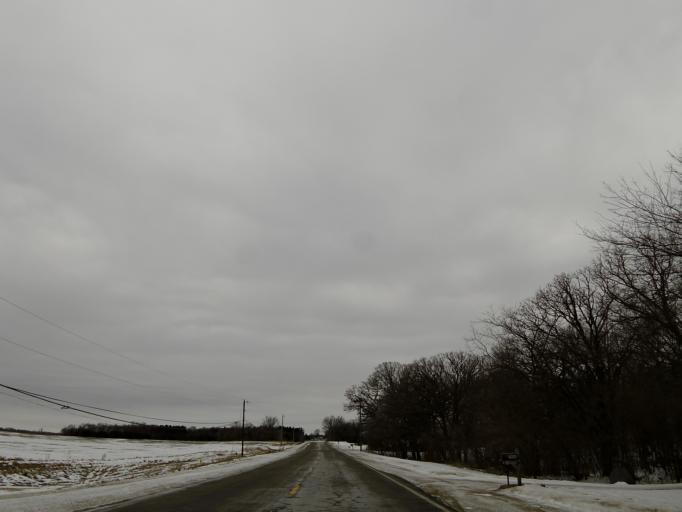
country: US
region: Minnesota
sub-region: Washington County
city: Cottage Grove
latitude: 44.8136
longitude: -92.8926
